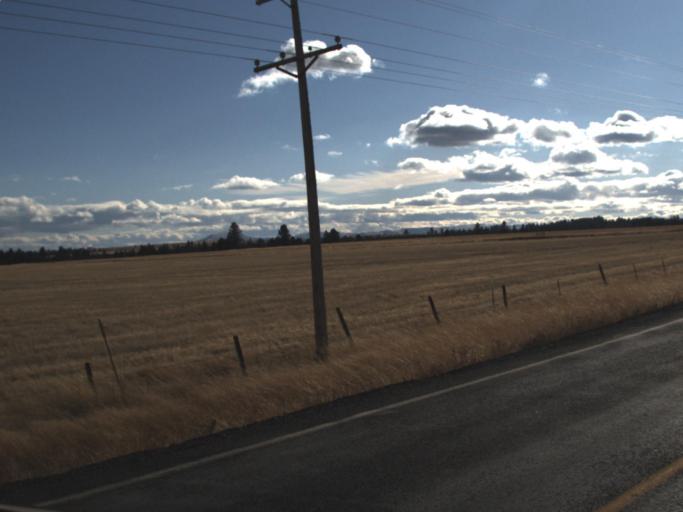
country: US
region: Washington
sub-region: Asotin County
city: Asotin
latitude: 46.1204
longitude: -117.1351
